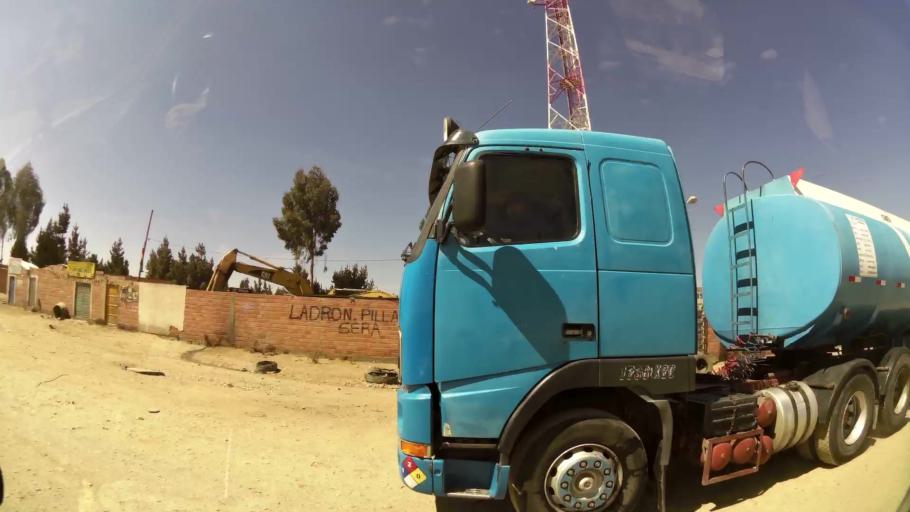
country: BO
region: La Paz
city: La Paz
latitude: -16.5507
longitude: -68.1838
